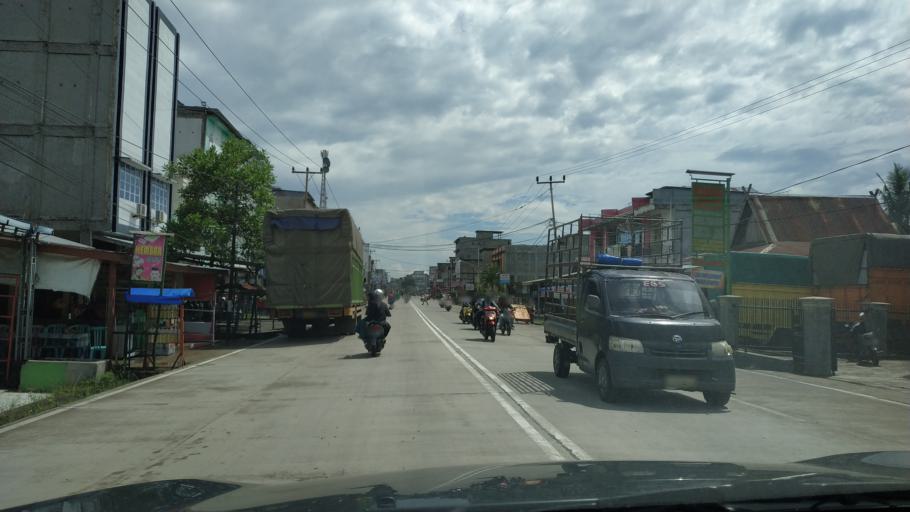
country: ID
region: Riau
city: Tembilahan
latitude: -0.3263
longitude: 103.1446
